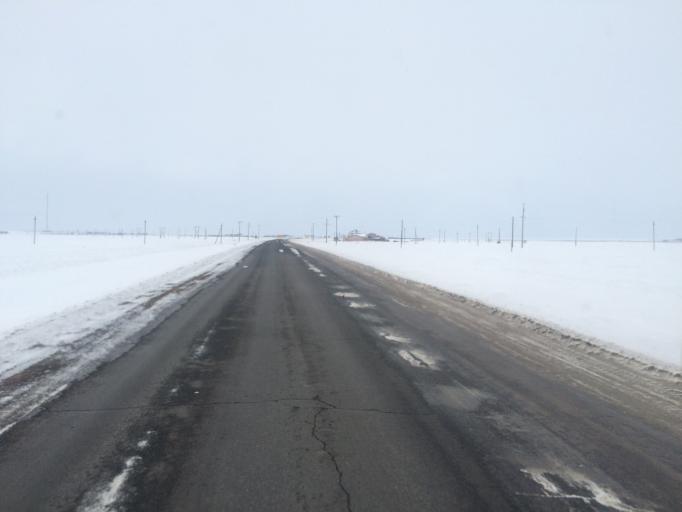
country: RU
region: Orenburg
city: Dombarovskiy
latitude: 49.9568
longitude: 60.0846
